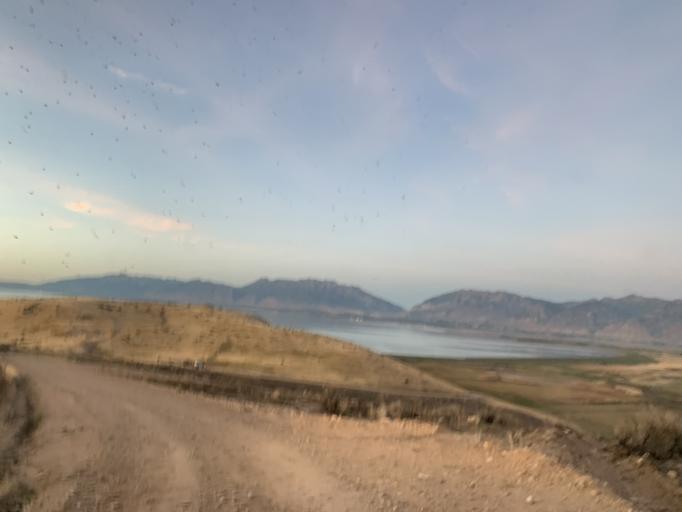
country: US
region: Utah
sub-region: Utah County
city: West Mountain
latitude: 40.1201
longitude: -111.8164
